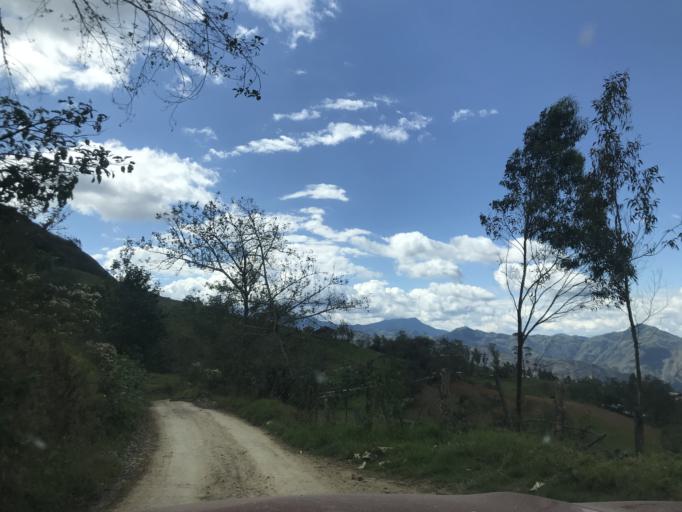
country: PE
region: Cajamarca
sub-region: Provincia de Chota
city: Querocoto
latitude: -6.3379
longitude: -79.0661
